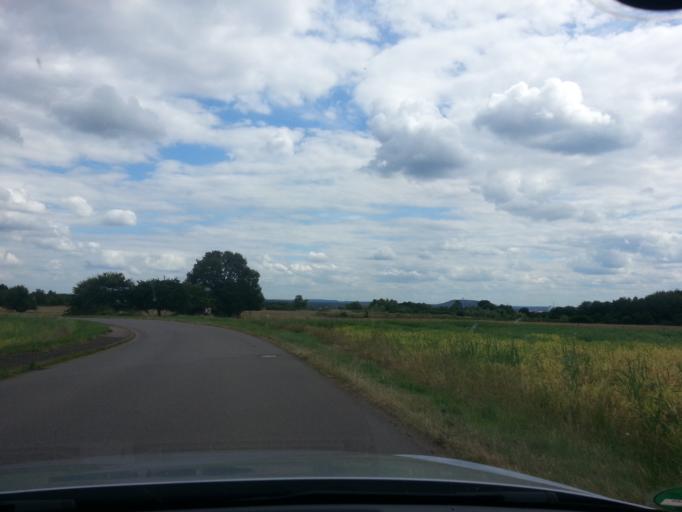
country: DE
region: Saarland
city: Nalbach
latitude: 49.3836
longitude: 6.7676
